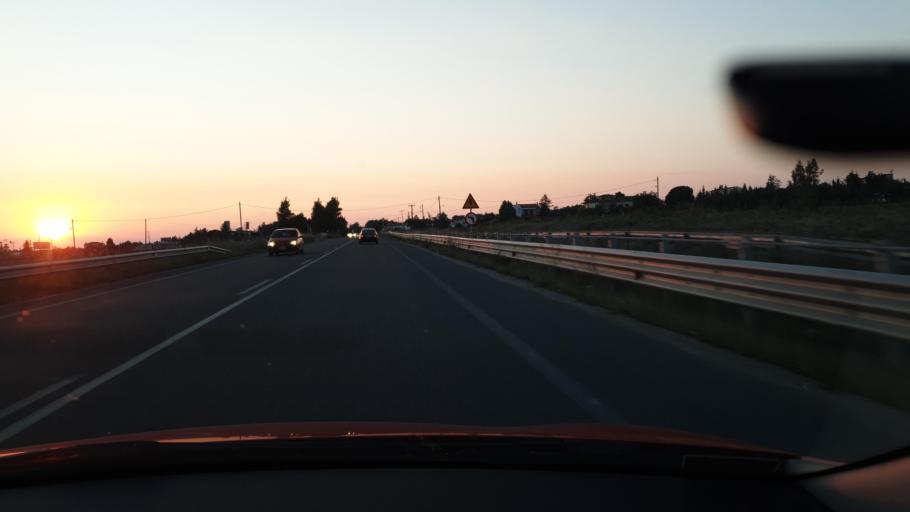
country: GR
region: Central Macedonia
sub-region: Nomos Thessalonikis
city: Agia Paraskevi
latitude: 40.5193
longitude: 23.0615
